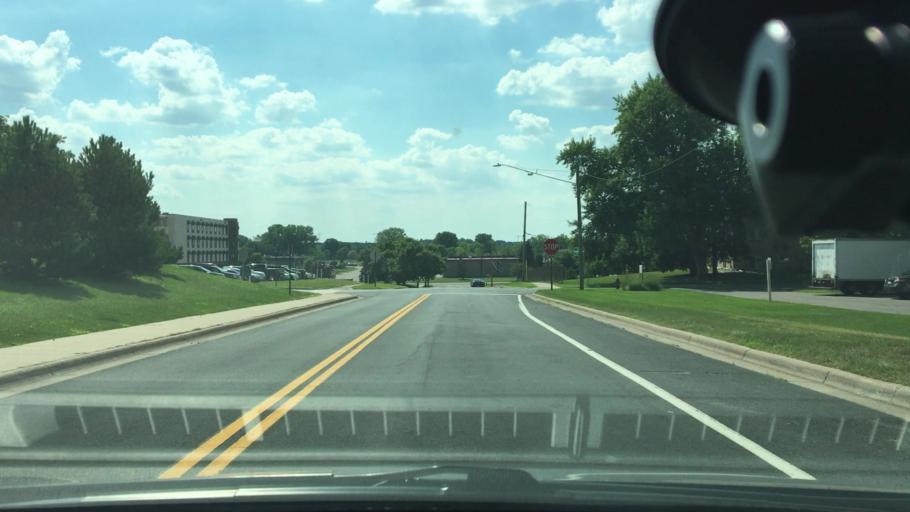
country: US
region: Minnesota
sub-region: Hennepin County
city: New Hope
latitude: 45.0548
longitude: -93.3874
